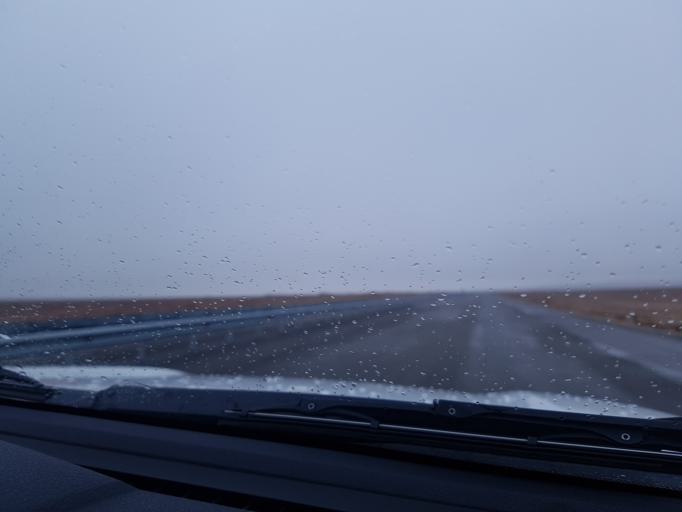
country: TM
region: Balkan
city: Balkanabat
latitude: 39.9725
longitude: 53.7951
